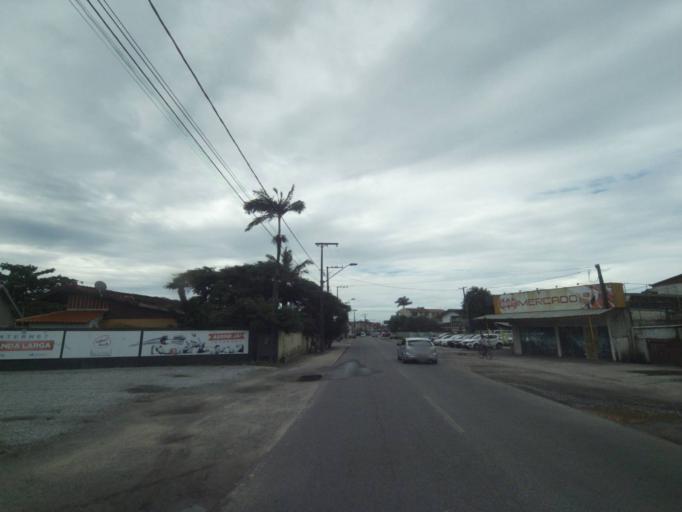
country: BR
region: Parana
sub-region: Guaratuba
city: Guaratuba
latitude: -25.8203
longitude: -48.5397
